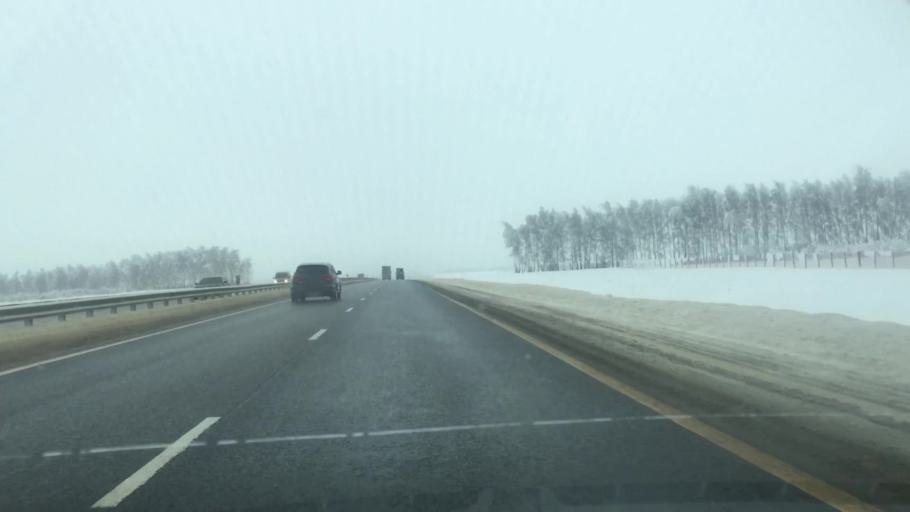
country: RU
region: Lipetsk
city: Stanovoye
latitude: 52.7938
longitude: 38.3384
